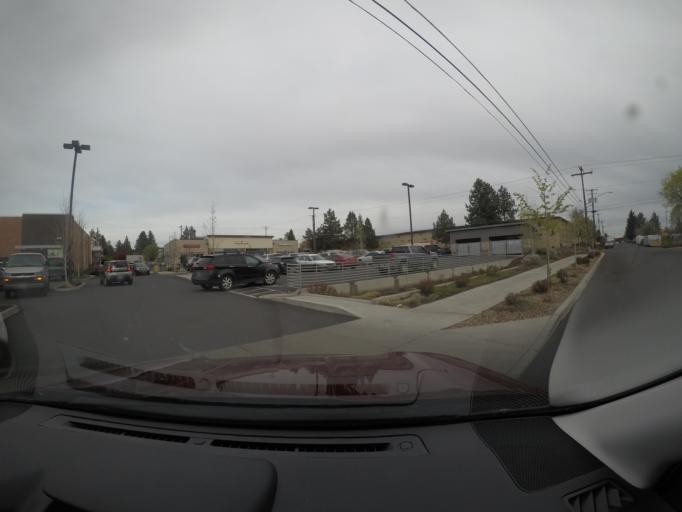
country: US
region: Oregon
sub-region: Deschutes County
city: Bend
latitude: 44.0554
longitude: -121.3039
